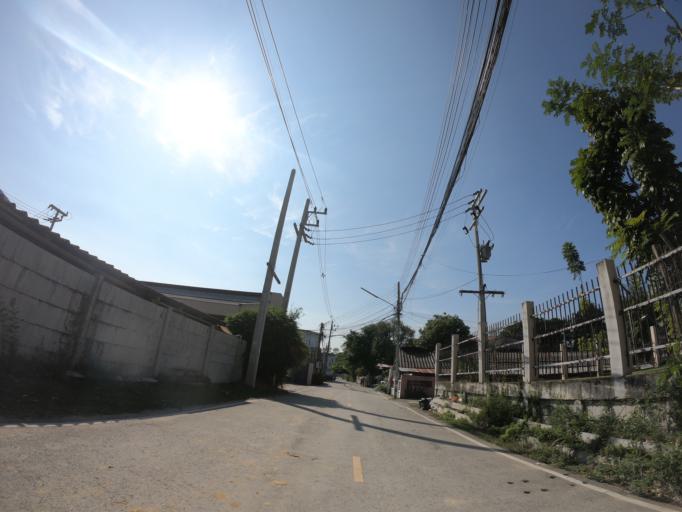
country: TH
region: Chiang Mai
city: Saraphi
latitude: 18.7591
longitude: 99.0320
